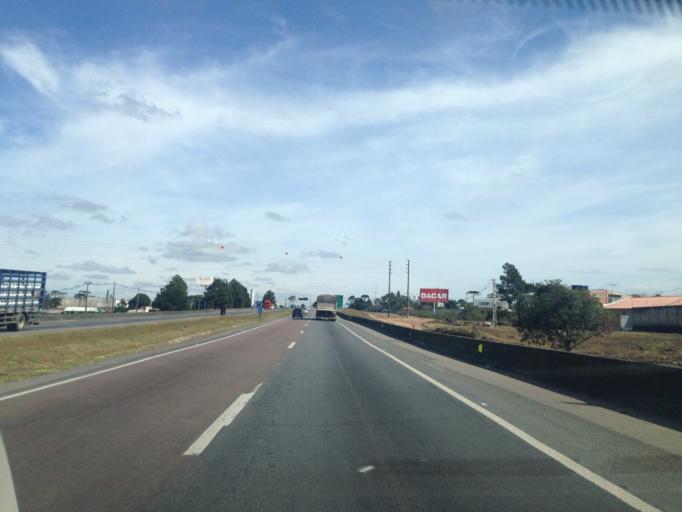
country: BR
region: Parana
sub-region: Sao Jose Dos Pinhais
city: Sao Jose dos Pinhais
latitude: -25.5664
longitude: -49.1684
